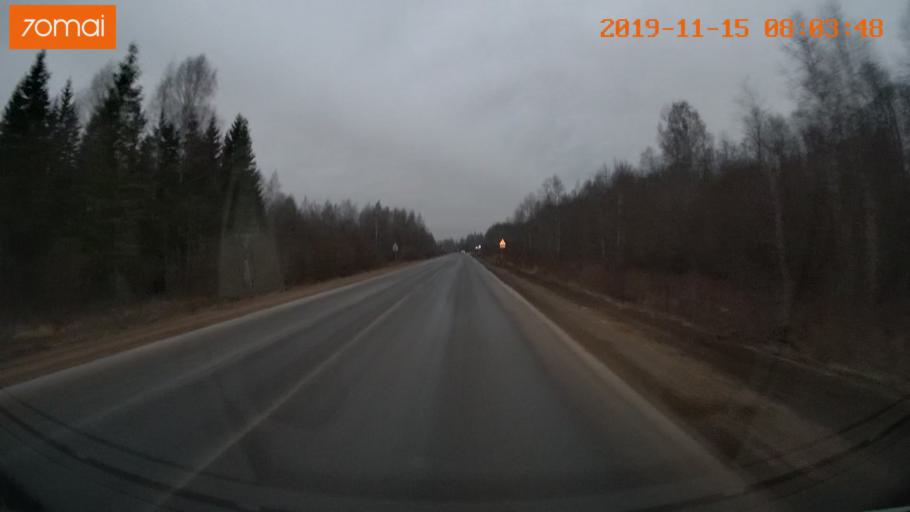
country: RU
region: Vologda
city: Cherepovets
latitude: 59.0016
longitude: 38.0846
